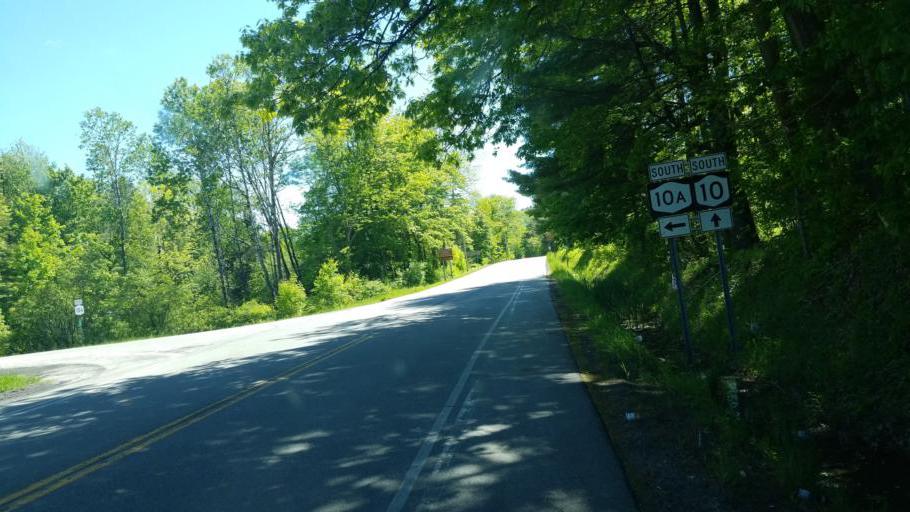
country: US
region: New York
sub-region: Fulton County
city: Johnstown
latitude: 43.0763
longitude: -74.5035
